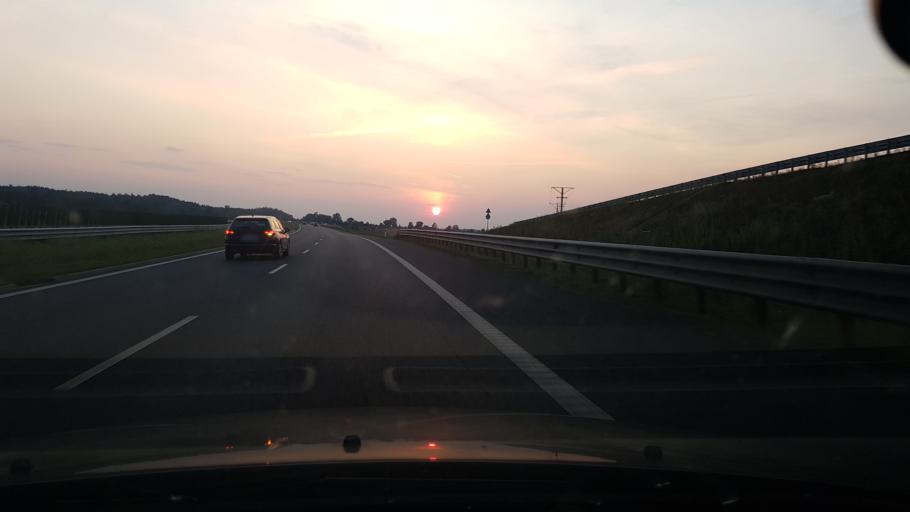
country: PL
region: Warmian-Masurian Voivodeship
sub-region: Powiat nidzicki
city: Nidzica
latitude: 53.3992
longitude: 20.3571
